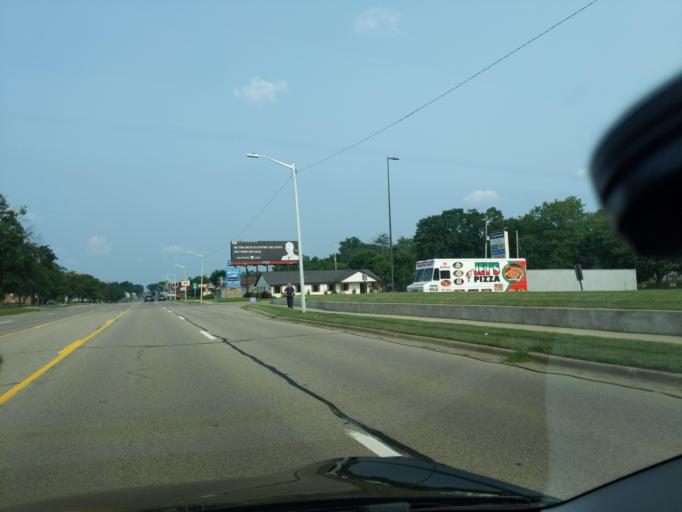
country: US
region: Michigan
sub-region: Jackson County
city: Jackson
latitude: 42.2475
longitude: -84.4402
